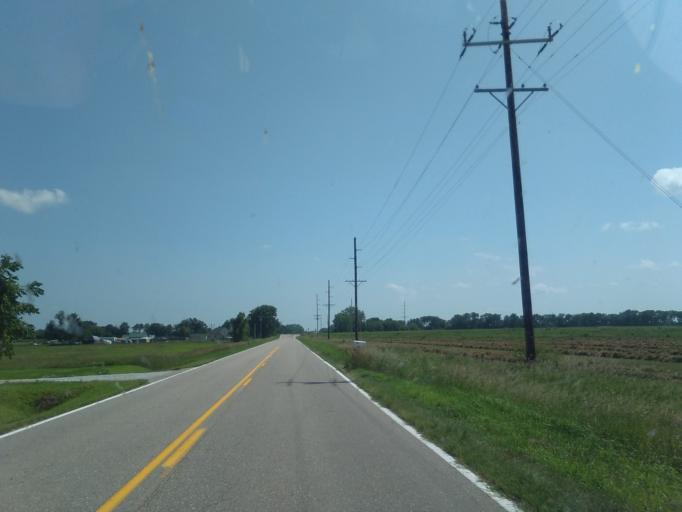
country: US
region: Nebraska
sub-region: Phelps County
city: Holdrege
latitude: 40.7139
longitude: -99.3794
